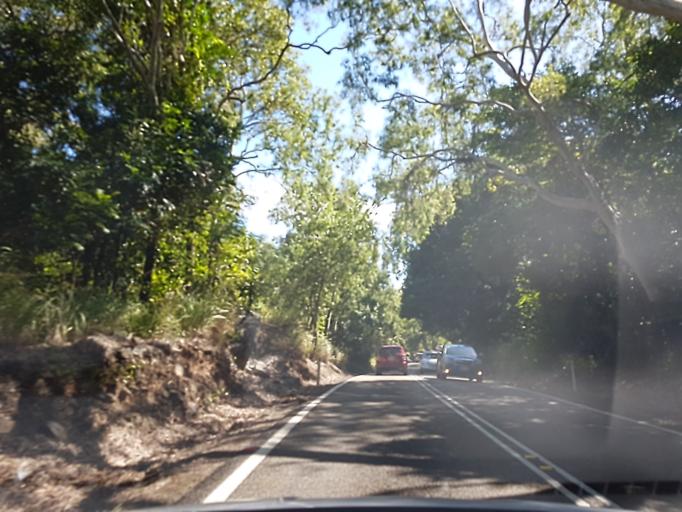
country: AU
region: Queensland
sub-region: Cairns
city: Port Douglas
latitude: -16.6096
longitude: 145.5293
